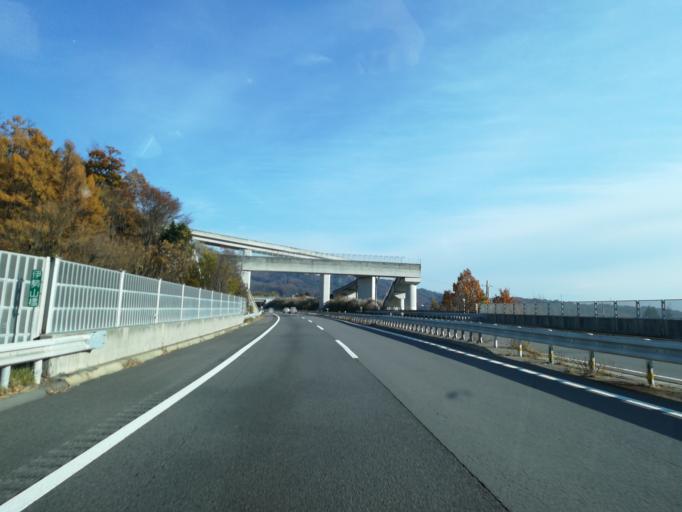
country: JP
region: Nagano
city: Ueda
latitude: 36.4100
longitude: 138.2898
